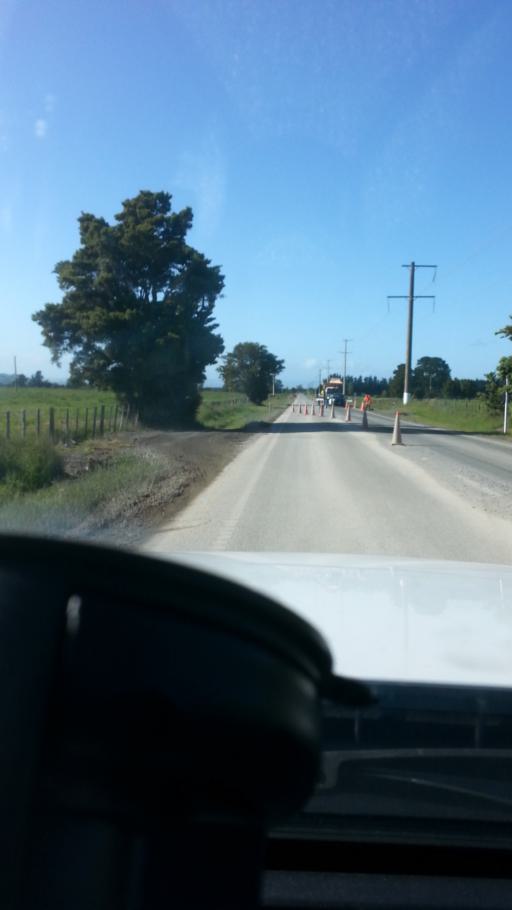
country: NZ
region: Wellington
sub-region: Masterton District
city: Masterton
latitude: -40.8137
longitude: 175.6230
